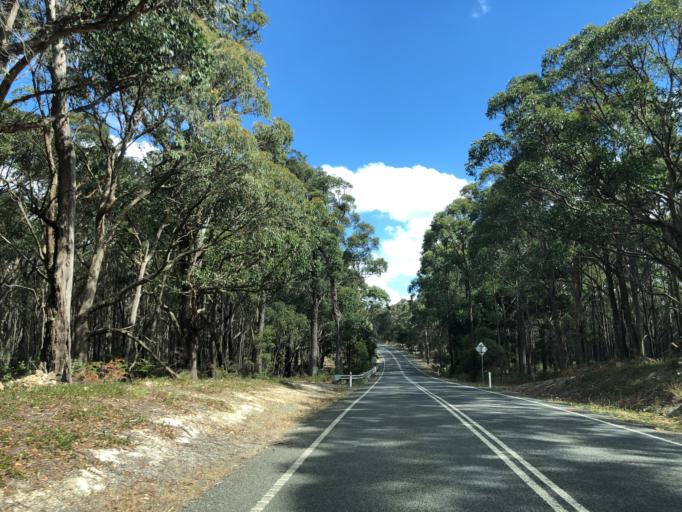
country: AU
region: Victoria
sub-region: Moorabool
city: Bacchus Marsh
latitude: -37.5033
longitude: 144.3115
